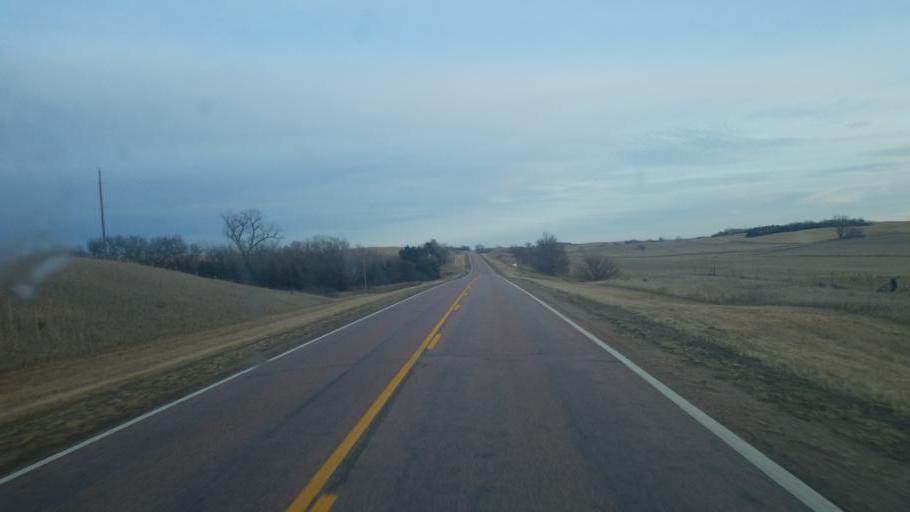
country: US
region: Nebraska
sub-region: Knox County
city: Bloomfield
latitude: 42.7278
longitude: -97.7198
